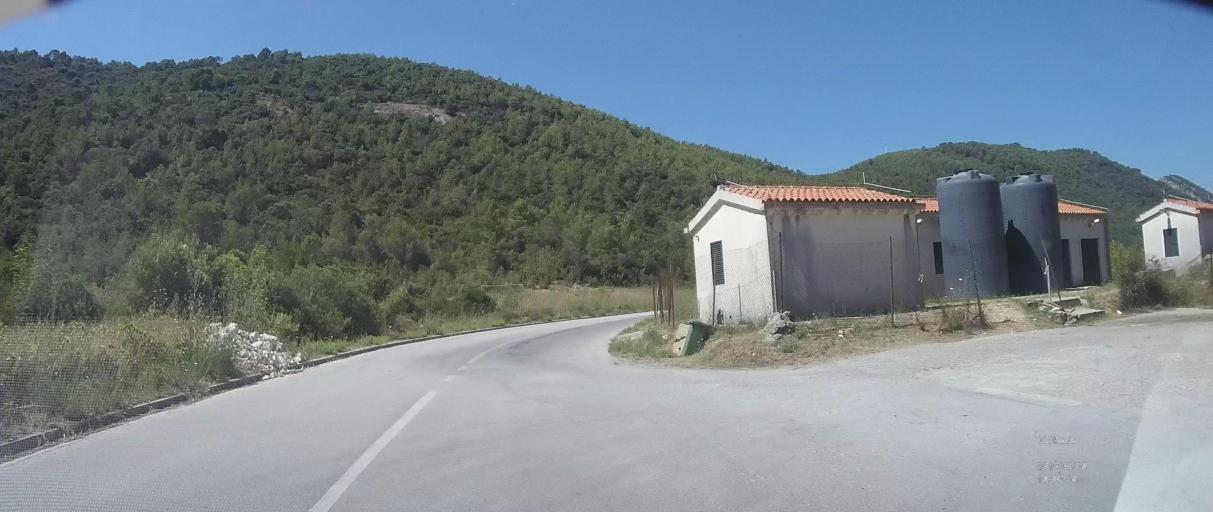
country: HR
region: Dubrovacko-Neretvanska
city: Blato
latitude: 42.7592
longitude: 17.4816
